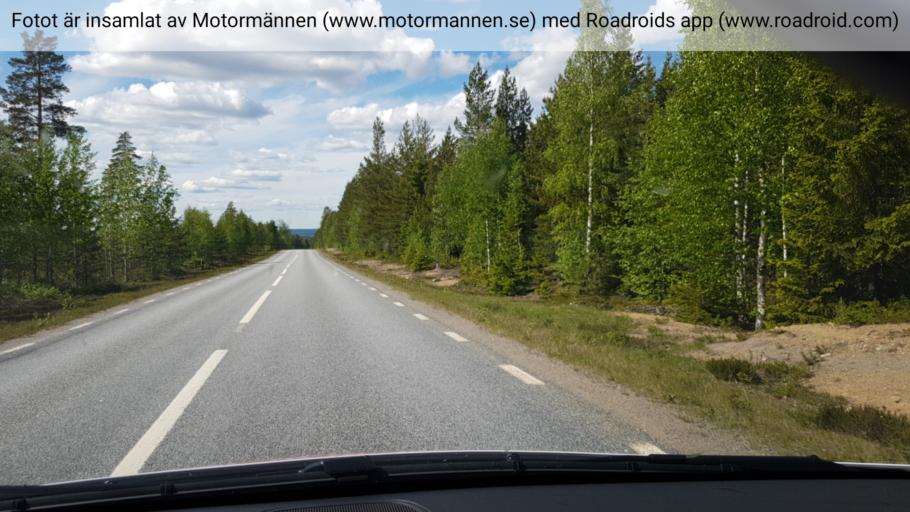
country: SE
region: Vaesterbotten
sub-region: Skelleftea Kommun
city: Burtraesk
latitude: 64.5041
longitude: 20.5114
